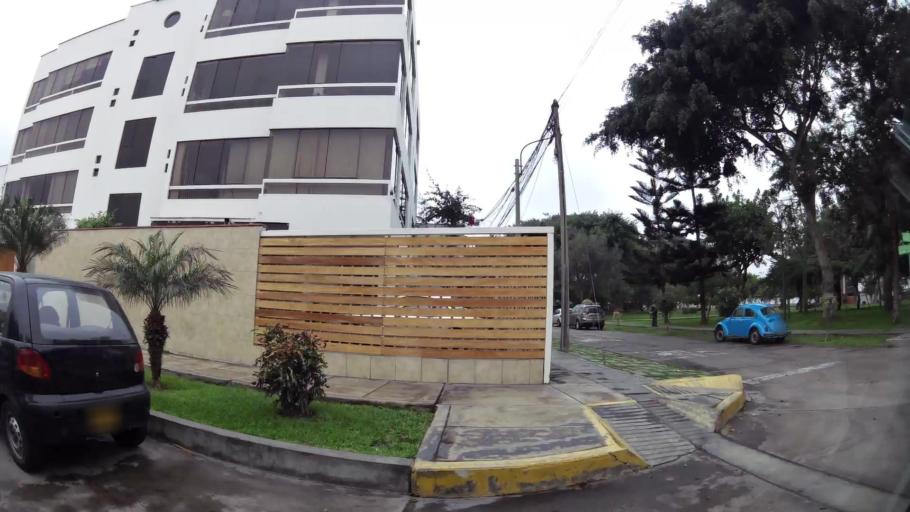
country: PE
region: Lima
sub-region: Lima
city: Surco
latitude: -12.1302
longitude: -77.0050
